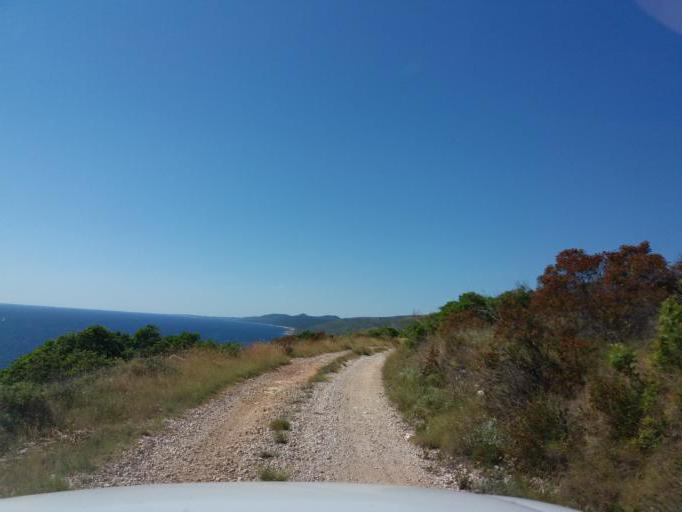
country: HR
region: Zadarska
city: Ugljan
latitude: 44.0139
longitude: 15.0298
